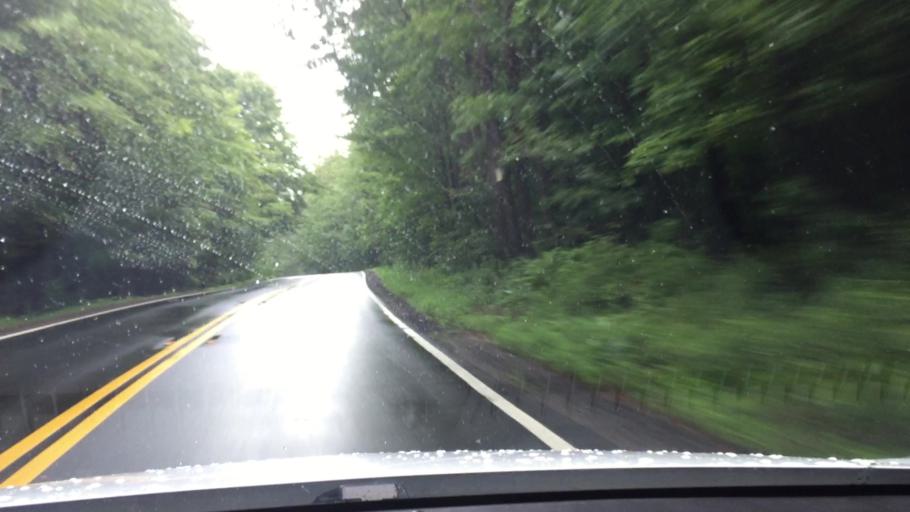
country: US
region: Massachusetts
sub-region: Berkshire County
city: Hinsdale
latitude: 42.4038
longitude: -73.1757
